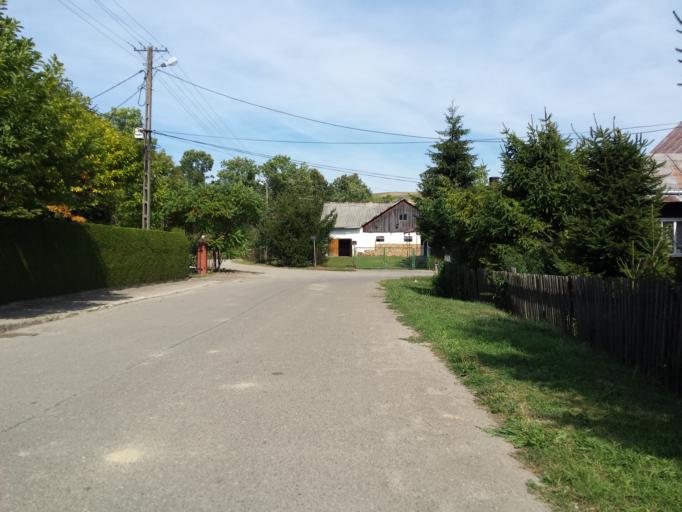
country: PL
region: Subcarpathian Voivodeship
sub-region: Powiat leski
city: Baligrod
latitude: 49.3378
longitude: 22.2853
